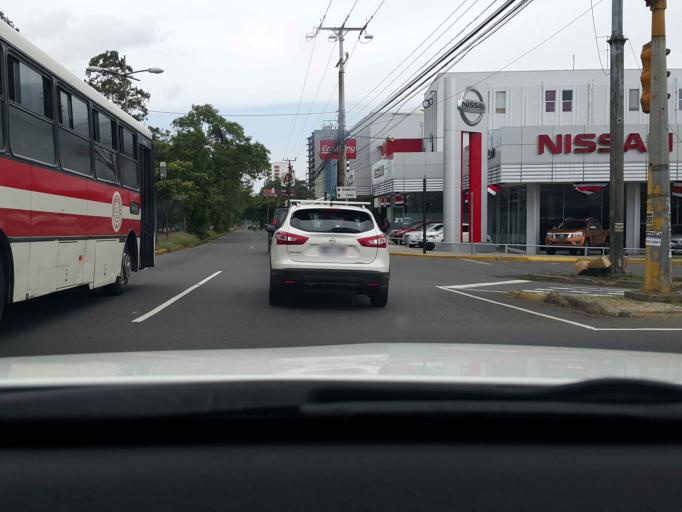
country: CR
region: San Jose
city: San Jose
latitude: 9.9380
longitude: -84.0983
